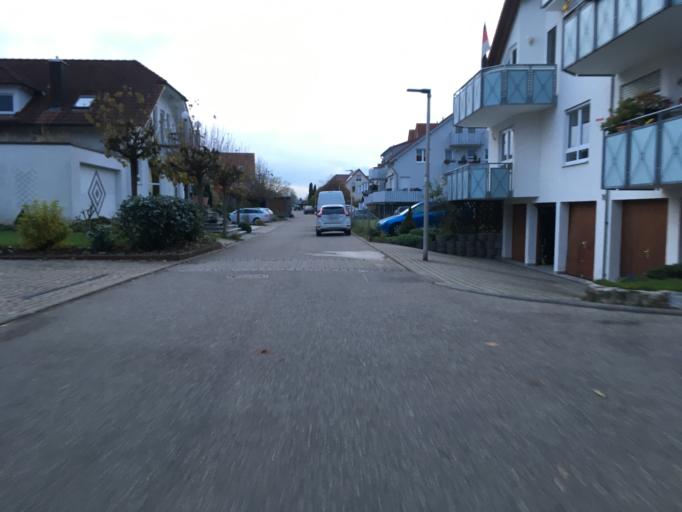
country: DE
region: Baden-Wuerttemberg
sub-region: Regierungsbezirk Stuttgart
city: Abstatt
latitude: 49.0662
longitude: 9.2873
